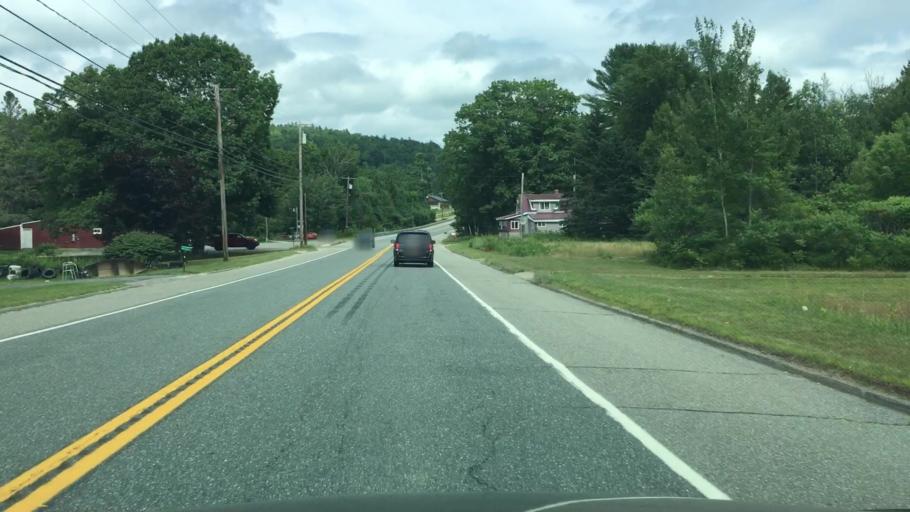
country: US
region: Maine
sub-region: Hancock County
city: Orland
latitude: 44.5658
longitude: -68.6859
